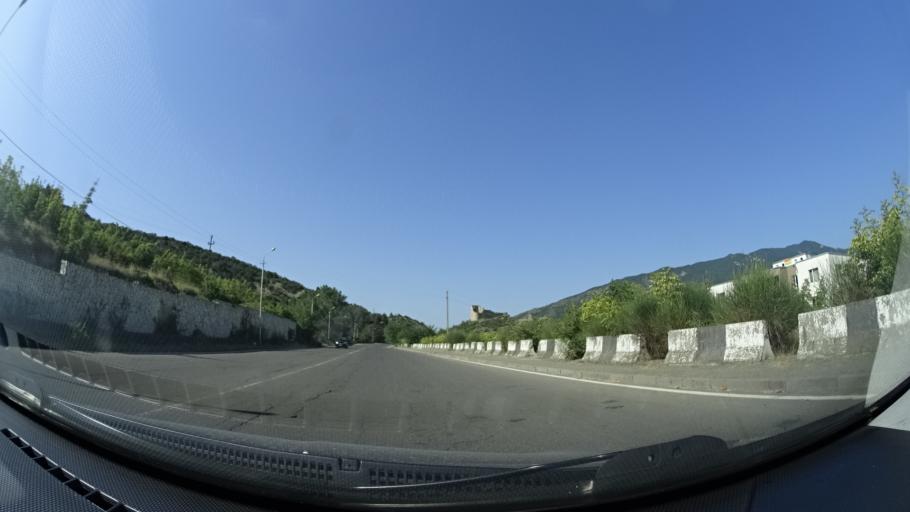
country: GE
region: Mtskheta-Mtianeti
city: Mtskheta
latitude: 41.8509
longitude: 44.7202
